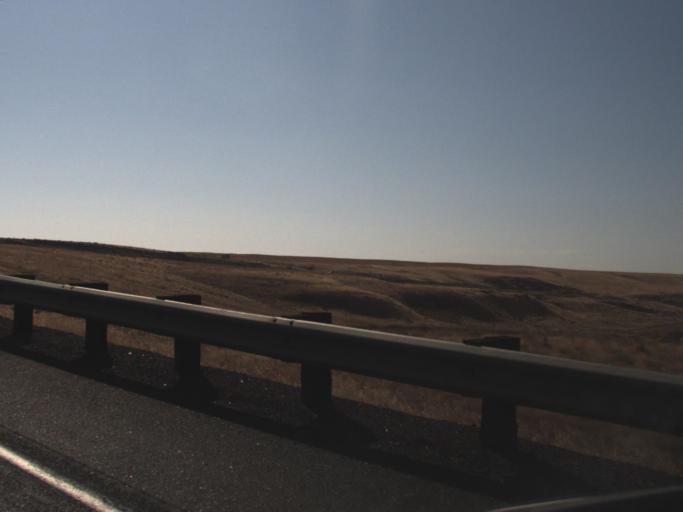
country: US
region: Washington
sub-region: Franklin County
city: Basin City
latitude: 46.5691
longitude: -119.0000
